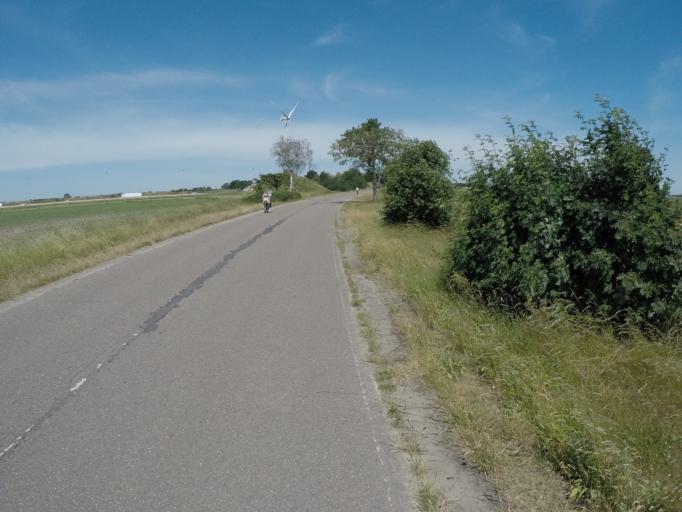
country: BE
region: Flanders
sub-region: Provincie Antwerpen
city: Brecht
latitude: 51.3758
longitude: 4.6621
